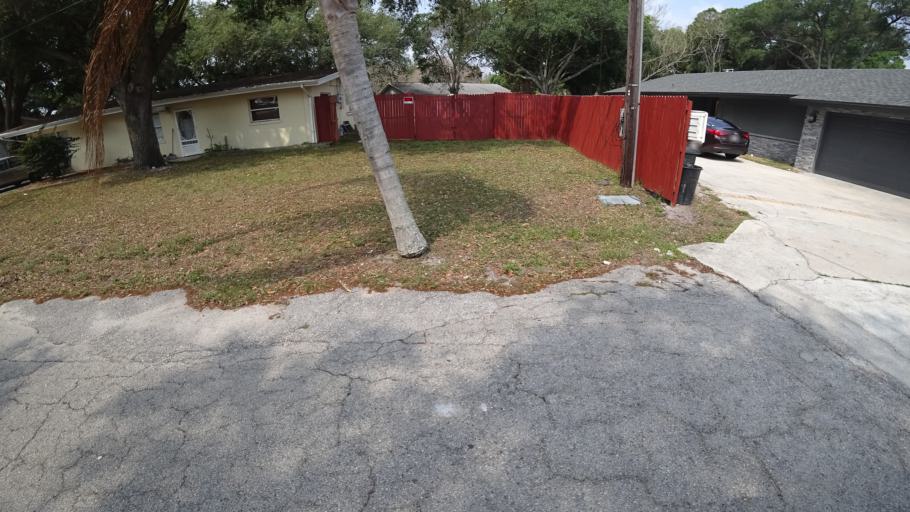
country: US
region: Florida
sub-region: Manatee County
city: Samoset
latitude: 27.4474
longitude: -82.5074
